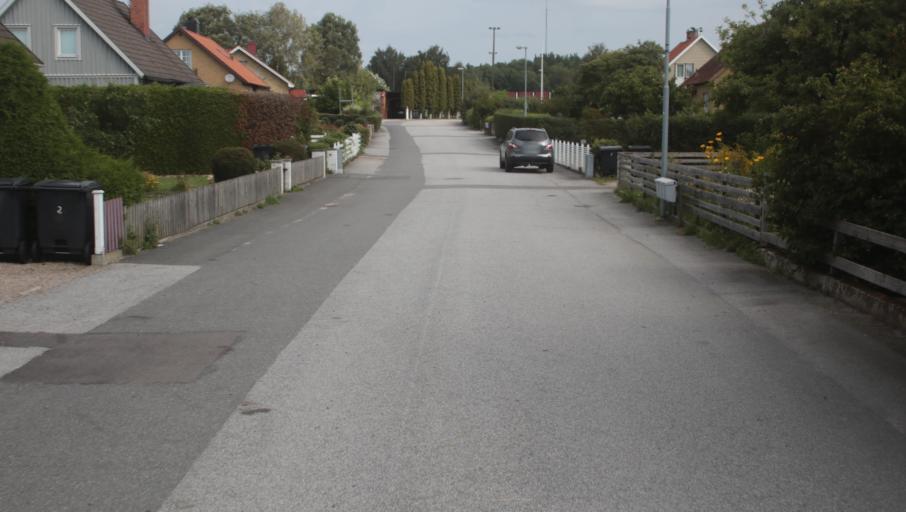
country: SE
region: Blekinge
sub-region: Karlshamns Kommun
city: Morrum
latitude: 56.1964
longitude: 14.7532
